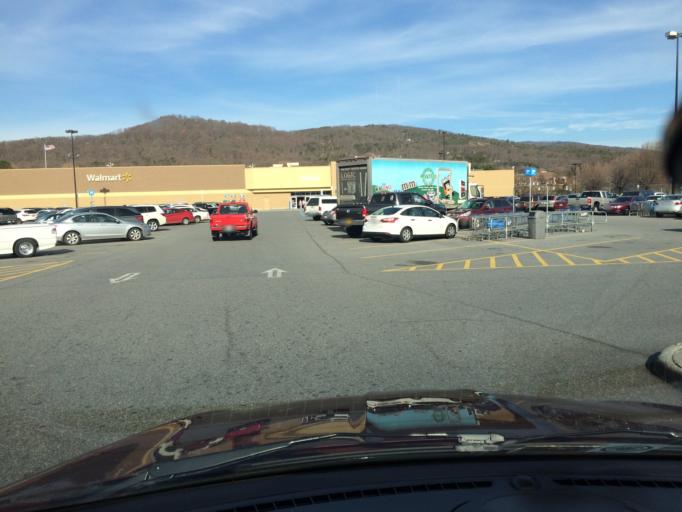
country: US
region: Virginia
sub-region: City of Salem
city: Salem
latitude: 37.2885
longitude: -80.0883
